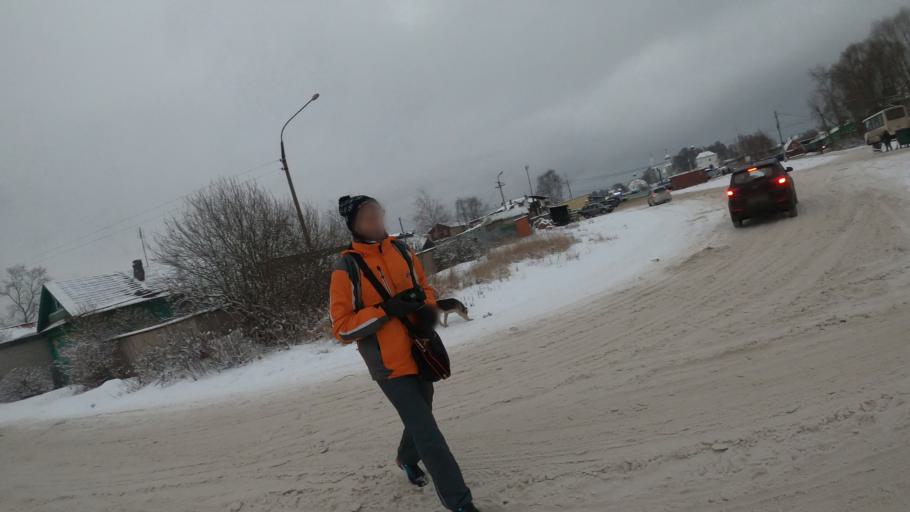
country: RU
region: Jaroslavl
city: Pereslavl'-Zalesskiy
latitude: 56.7242
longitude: 38.8337
